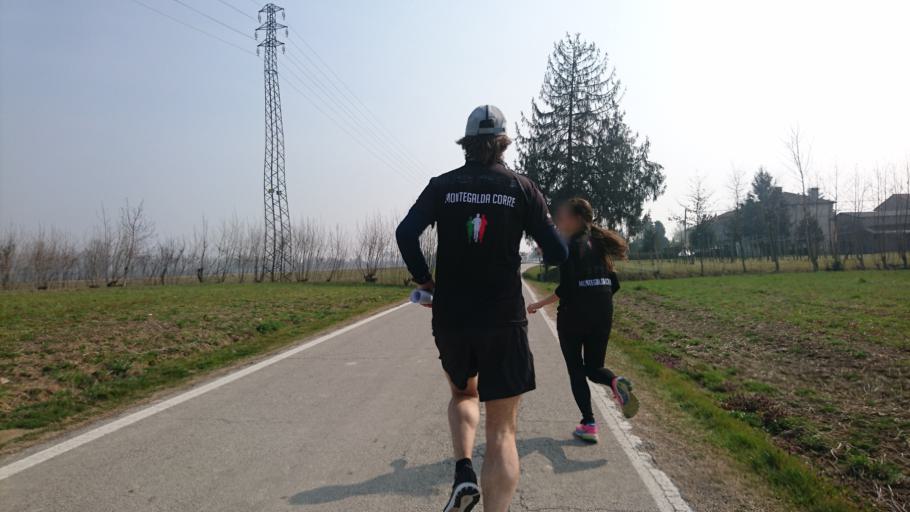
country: IT
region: Veneto
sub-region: Provincia di Vicenza
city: Montegalda
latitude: 45.4742
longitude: 11.6703
